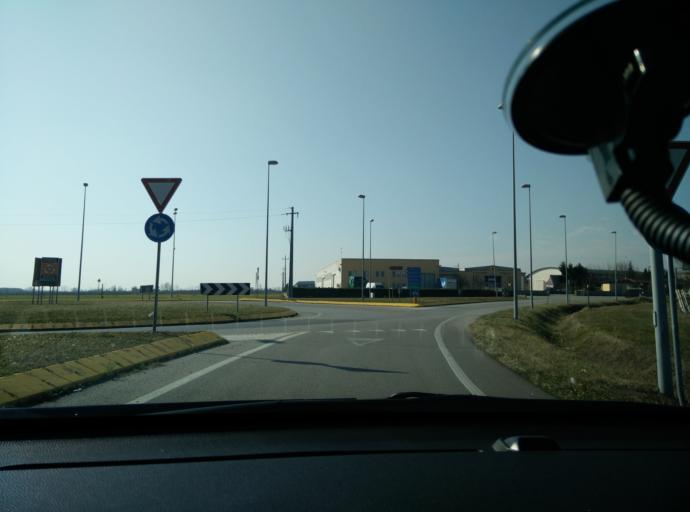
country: IT
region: Veneto
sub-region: Provincia di Treviso
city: San Michele di Piave
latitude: 45.8168
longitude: 12.3355
